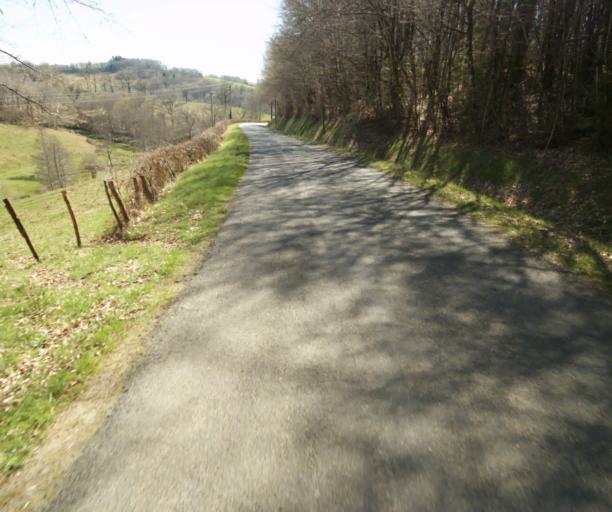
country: FR
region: Limousin
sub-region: Departement de la Correze
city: Chamboulive
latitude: 45.4559
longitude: 1.6735
